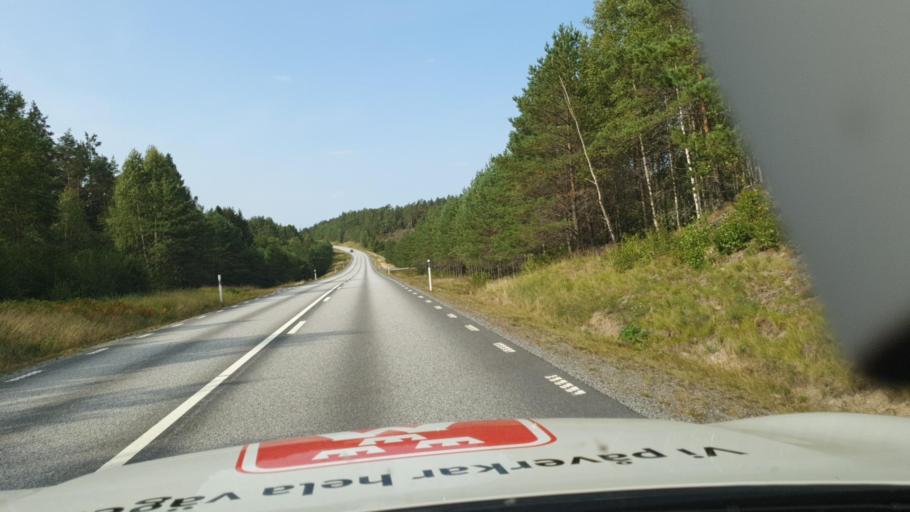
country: SE
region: Vaestra Goetaland
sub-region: Dals-Ed Kommun
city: Ed
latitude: 58.8459
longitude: 11.6724
